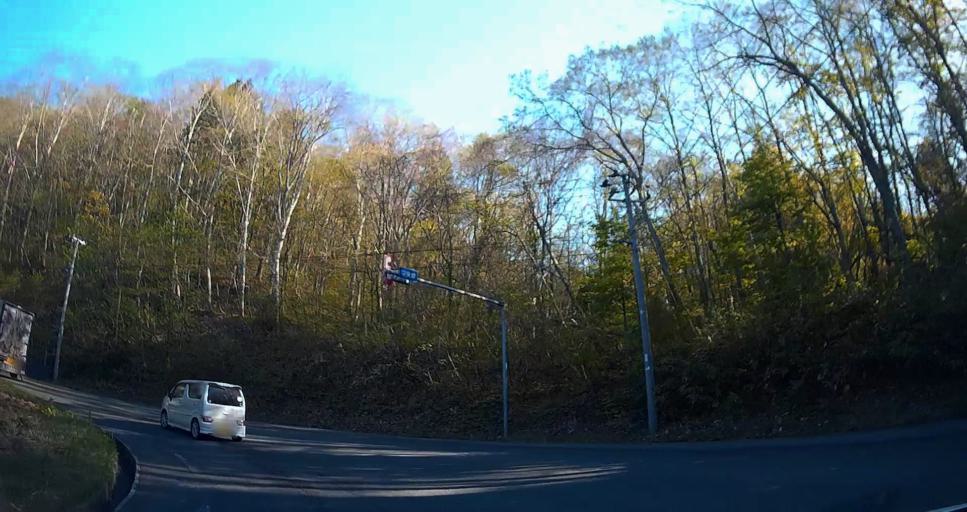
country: JP
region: Aomori
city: Mutsu
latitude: 41.4335
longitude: 141.1323
